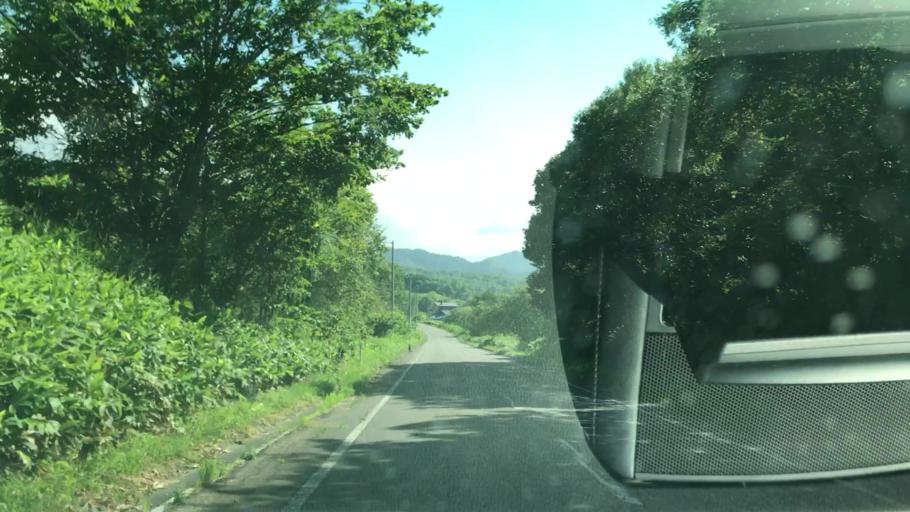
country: JP
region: Hokkaido
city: Shimo-furano
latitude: 42.8593
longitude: 142.4404
